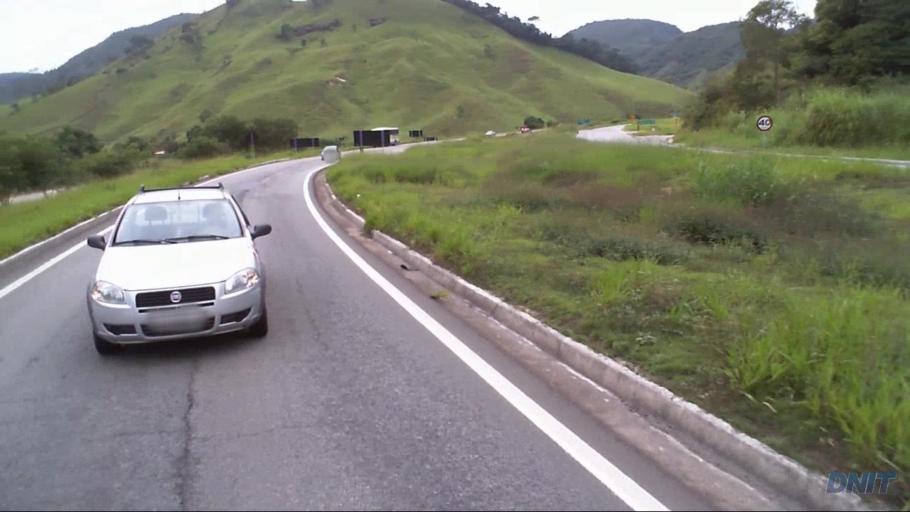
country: BR
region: Minas Gerais
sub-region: Timoteo
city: Timoteo
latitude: -19.6182
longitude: -42.8507
